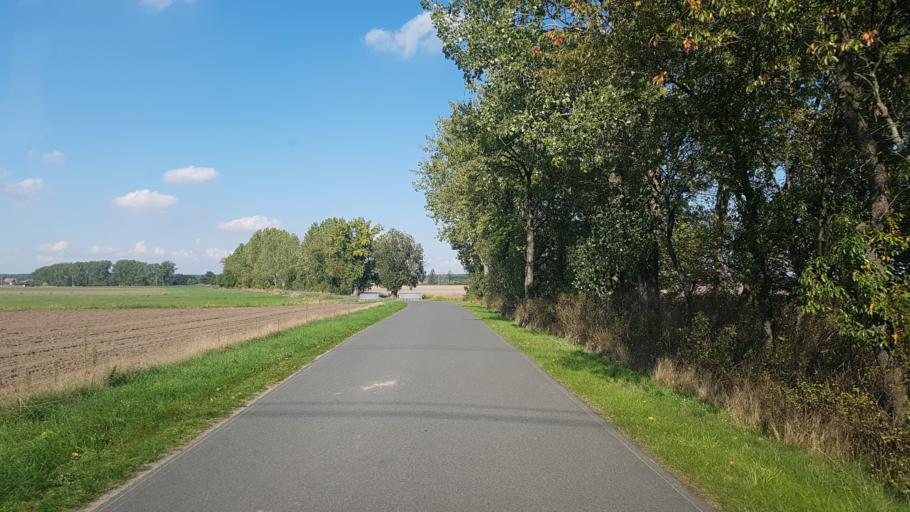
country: DE
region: Brandenburg
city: Ihlow
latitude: 51.8376
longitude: 13.2834
